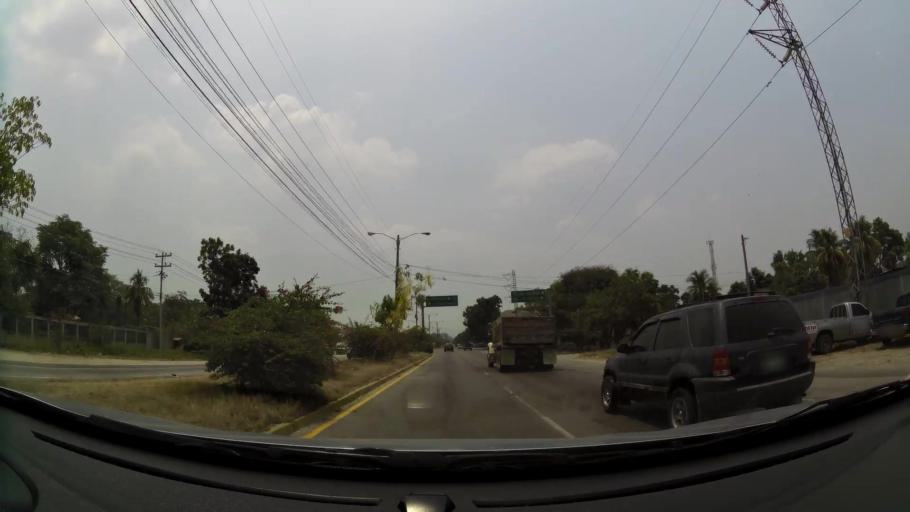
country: HN
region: Cortes
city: San Pedro Sula
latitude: 15.4760
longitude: -87.9725
